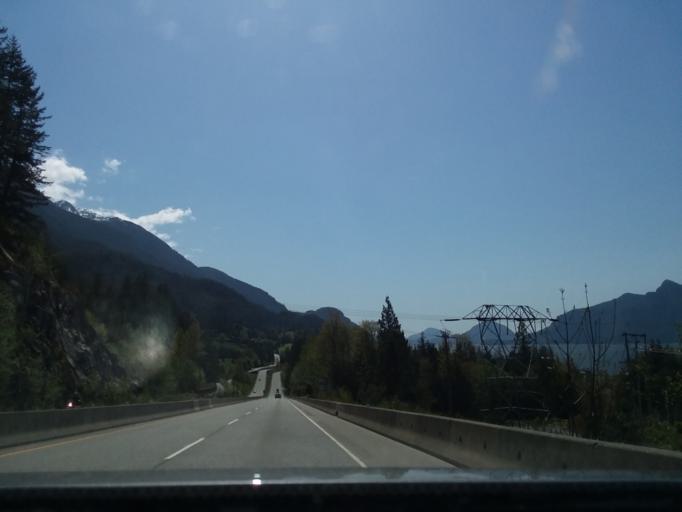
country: CA
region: British Columbia
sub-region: Greater Vancouver Regional District
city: Lions Bay
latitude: 49.5884
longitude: -123.2198
